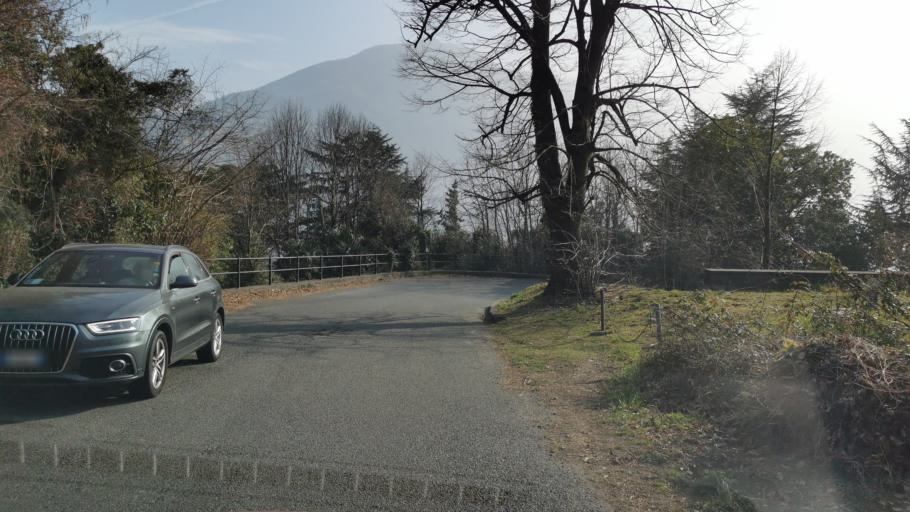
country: IT
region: Lombardy
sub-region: Provincia di Como
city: Tremezzo
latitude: 45.9836
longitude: 9.2224
